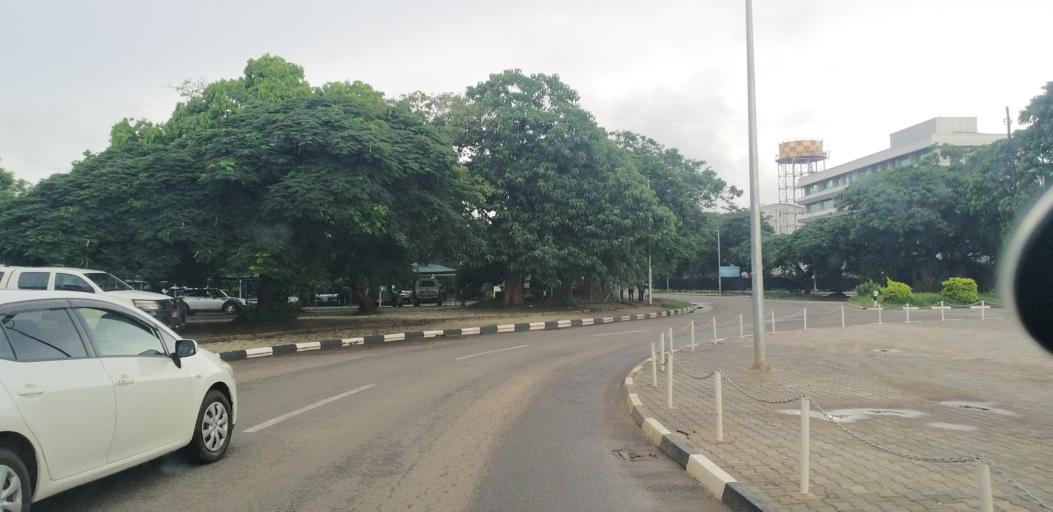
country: ZM
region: Lusaka
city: Lusaka
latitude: -15.4226
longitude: 28.3092
